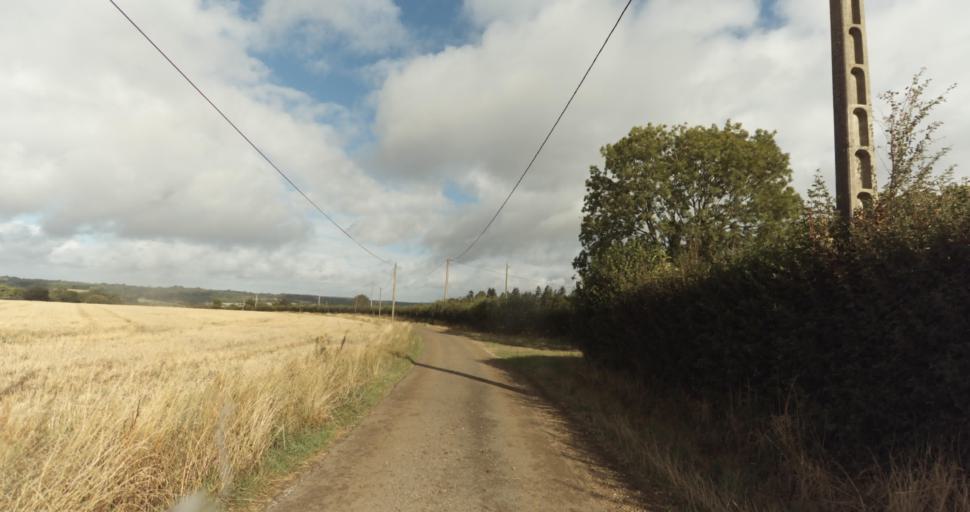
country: FR
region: Lower Normandy
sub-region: Departement de l'Orne
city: Gace
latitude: 48.8607
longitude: 0.2987
